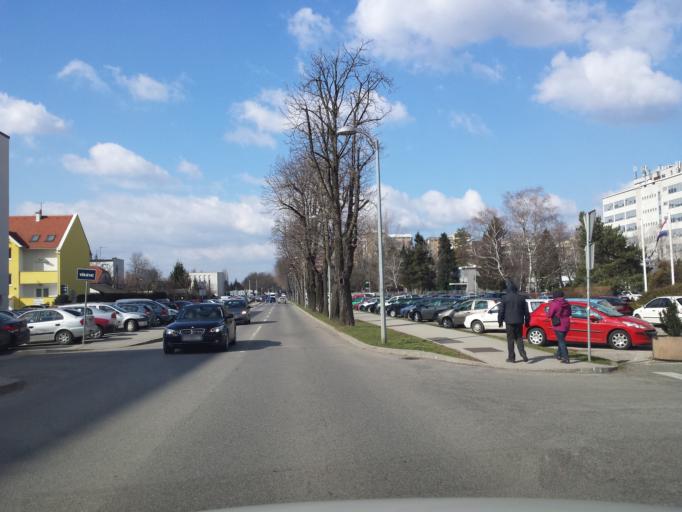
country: HR
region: Grad Zagreb
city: Jankomir
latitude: 45.8007
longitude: 15.9350
